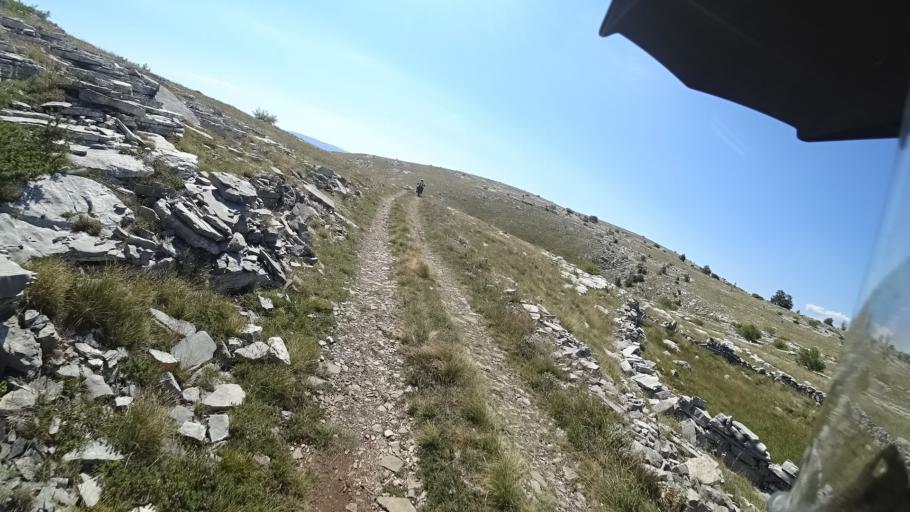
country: HR
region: Splitsko-Dalmatinska
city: Hrvace
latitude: 43.9021
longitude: 16.5918
